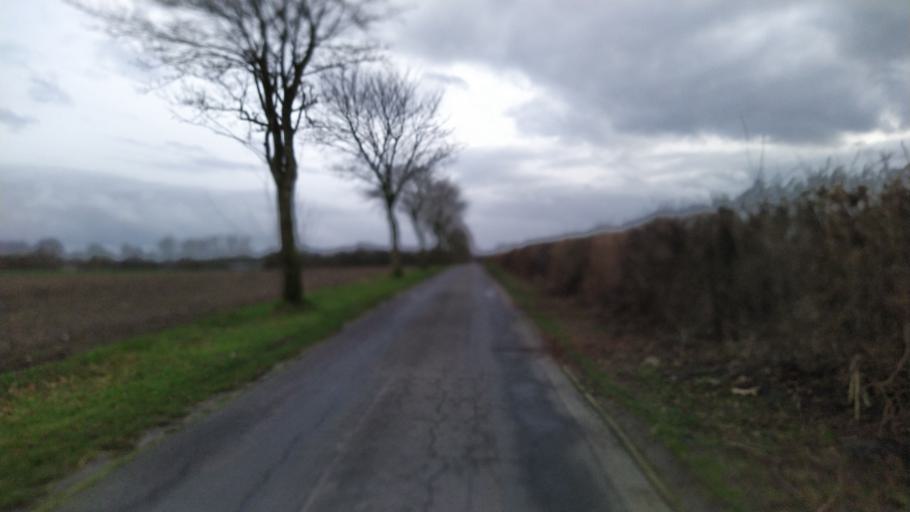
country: DE
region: Lower Saxony
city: Bargstedt
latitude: 53.4439
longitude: 9.4671
